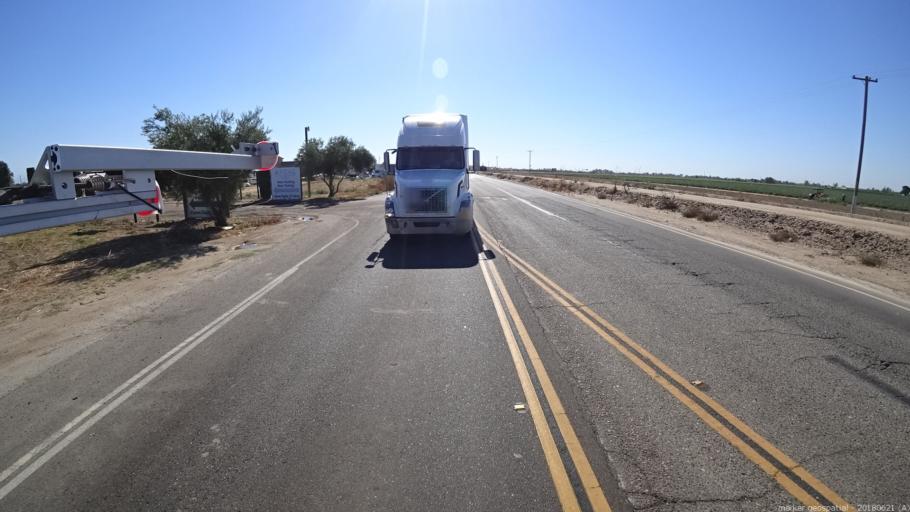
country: US
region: California
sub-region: Fresno County
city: Biola
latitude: 36.8513
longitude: -119.9520
